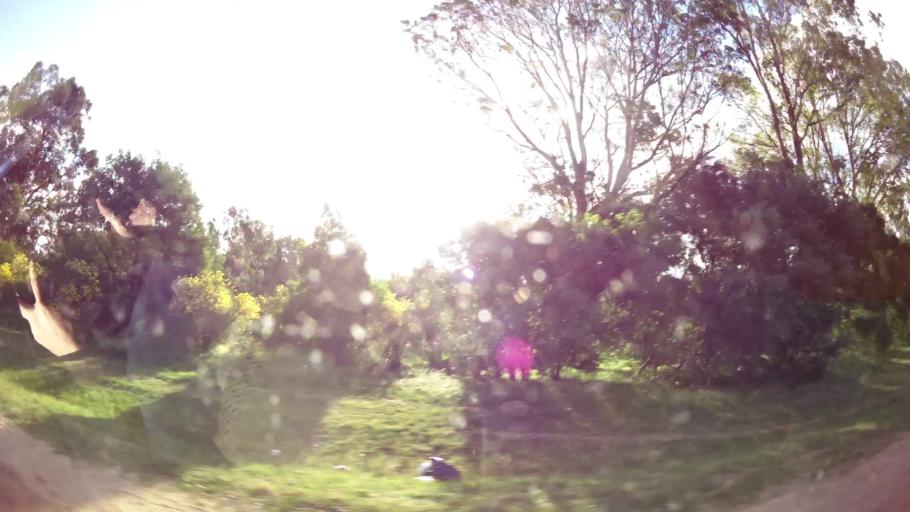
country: UY
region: Montevideo
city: Montevideo
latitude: -34.8969
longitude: -56.2613
